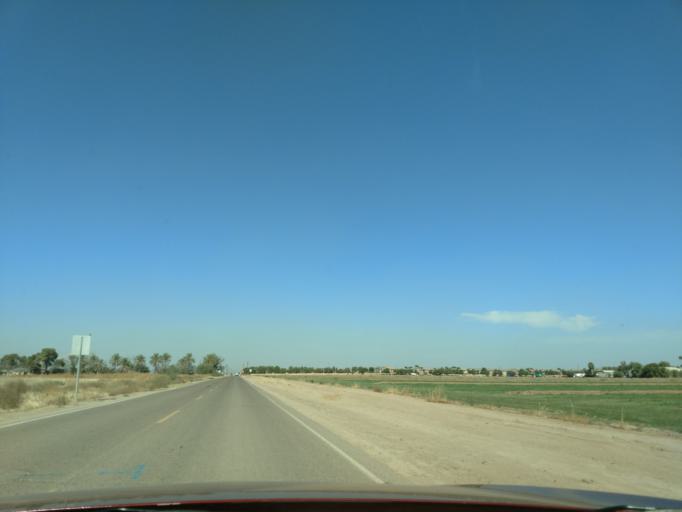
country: US
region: Arizona
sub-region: Maricopa County
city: Laveen
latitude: 33.3583
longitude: -112.1863
